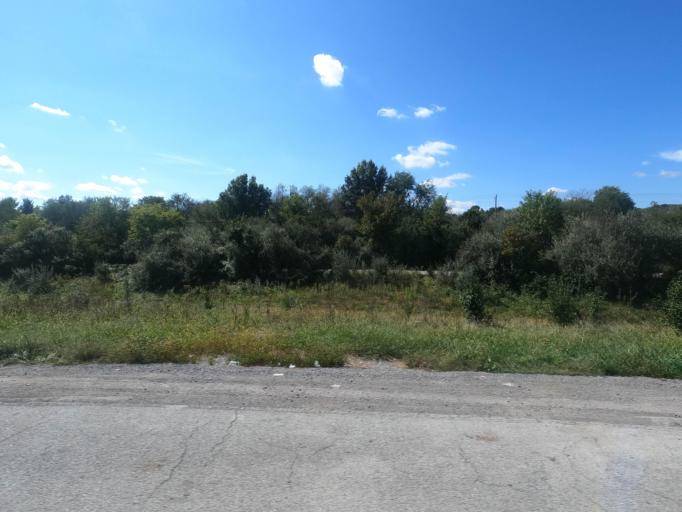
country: US
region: Illinois
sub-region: Jefferson County
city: Mount Vernon
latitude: 38.3602
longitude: -89.0363
